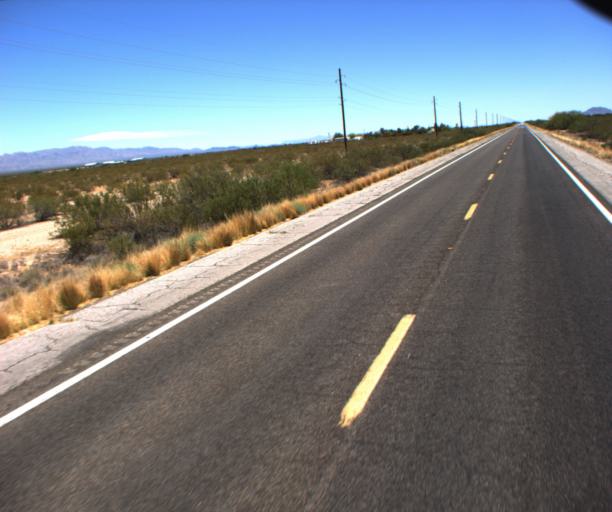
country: US
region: Arizona
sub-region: La Paz County
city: Salome
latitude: 33.8331
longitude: -113.5002
